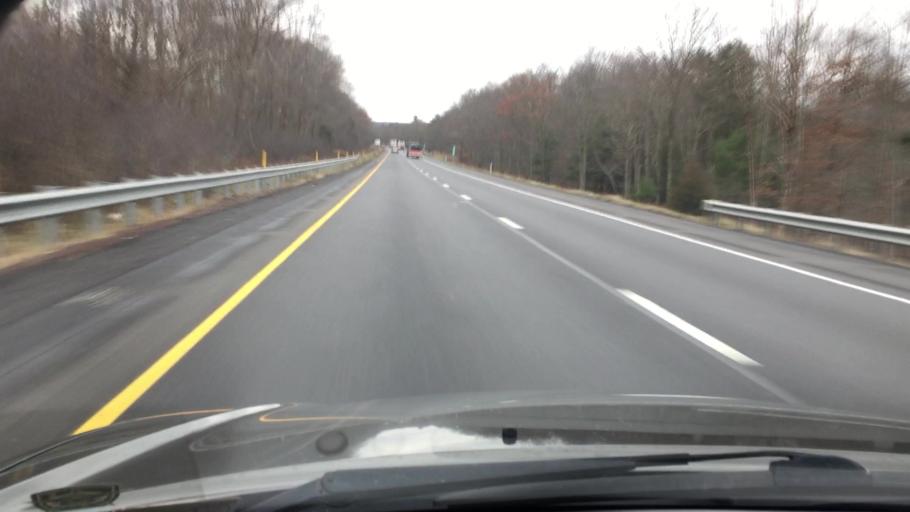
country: US
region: Pennsylvania
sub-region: Luzerne County
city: White Haven
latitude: 41.0562
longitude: -75.8254
